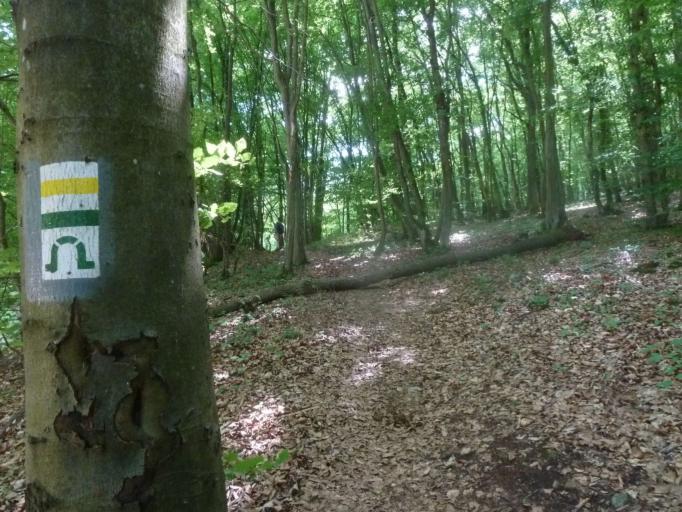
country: HU
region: Borsod-Abauj-Zemplen
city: Rudabanya
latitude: 48.4782
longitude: 20.5444
